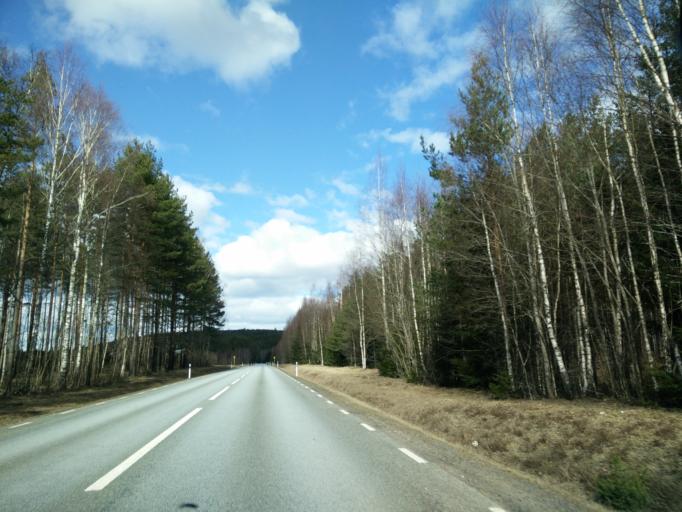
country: SE
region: Vaermland
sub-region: Munkfors Kommun
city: Munkfors
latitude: 59.9392
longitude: 13.5797
